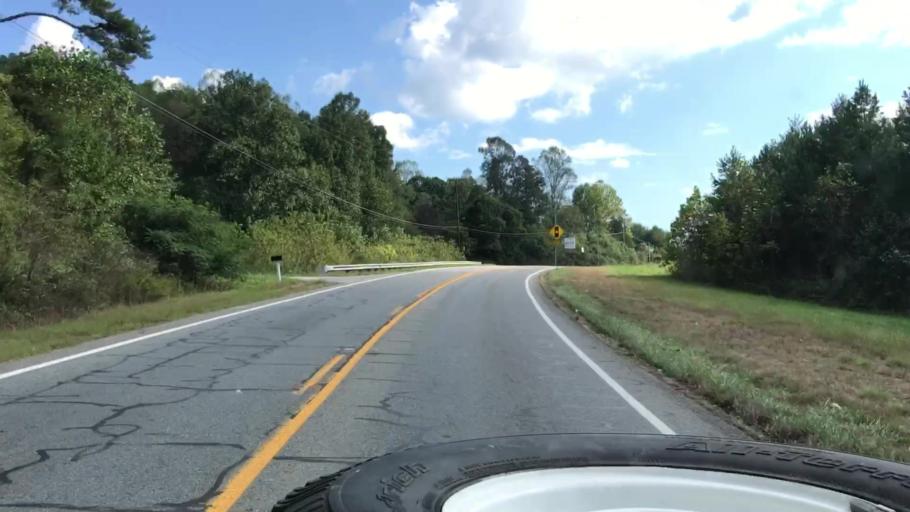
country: US
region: Georgia
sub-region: Fannin County
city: Blue Ridge
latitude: 34.8786
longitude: -84.3236
